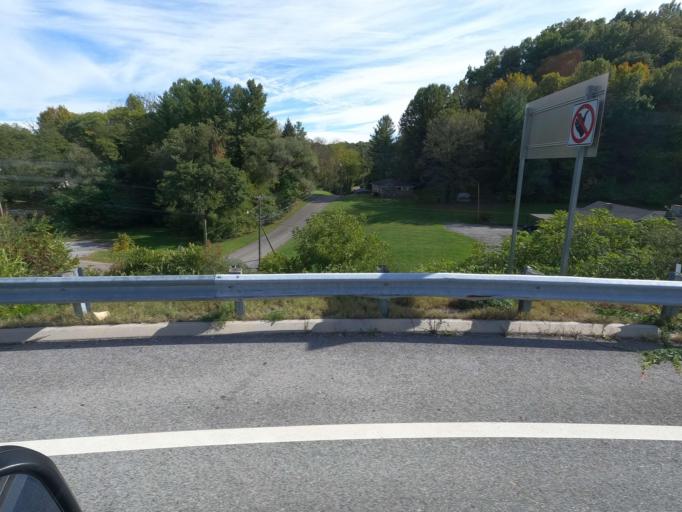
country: US
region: Tennessee
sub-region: Sullivan County
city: Bristol
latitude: 36.6021
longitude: -82.2270
